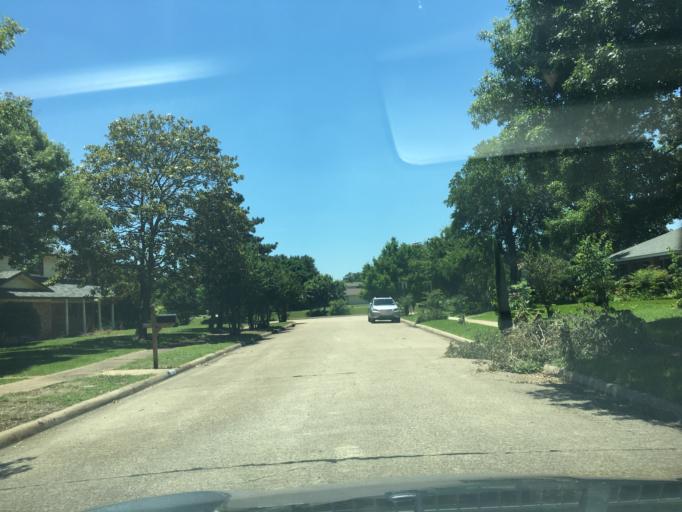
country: US
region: Texas
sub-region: Dallas County
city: Richardson
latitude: 32.9502
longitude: -96.6859
